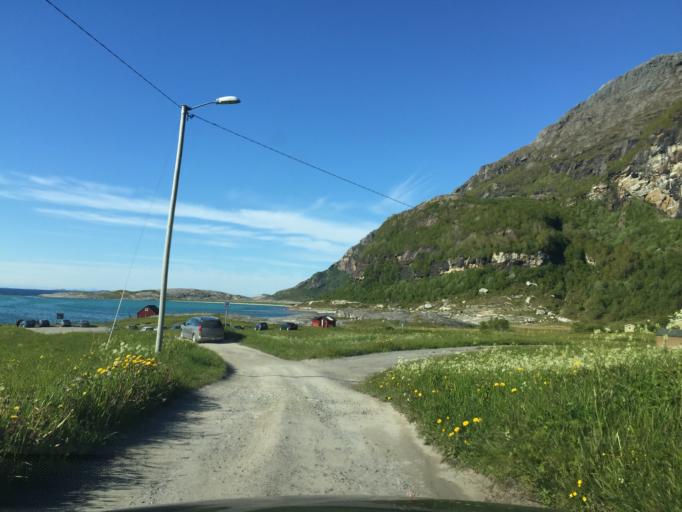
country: NO
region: Nordland
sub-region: Bodo
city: Loding
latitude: 67.4103
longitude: 14.6285
